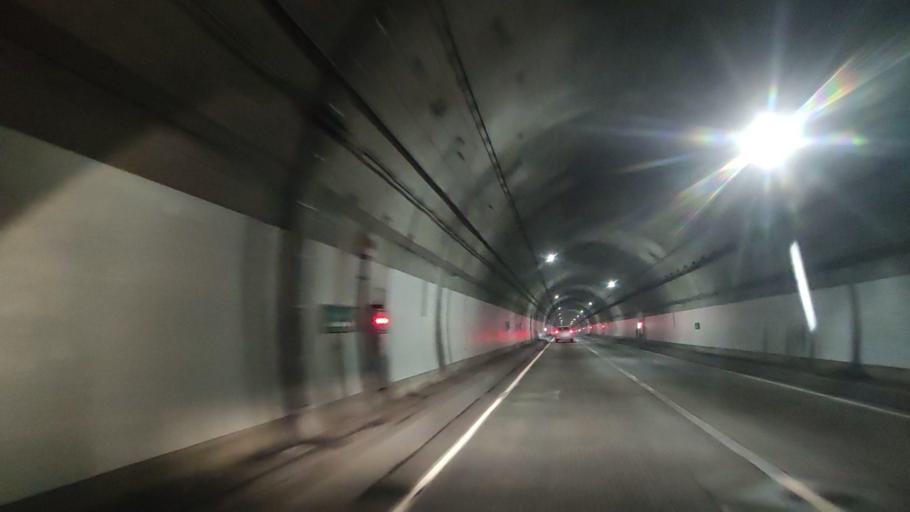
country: JP
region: Hokkaido
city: Rumoi
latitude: 43.7093
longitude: 141.3330
